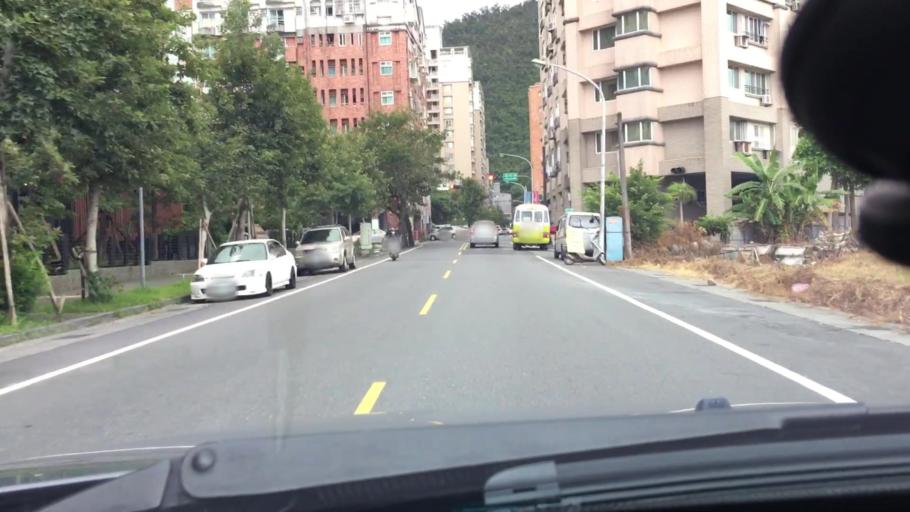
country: TW
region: Taiwan
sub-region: Yilan
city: Yilan
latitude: 24.8228
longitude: 121.7653
